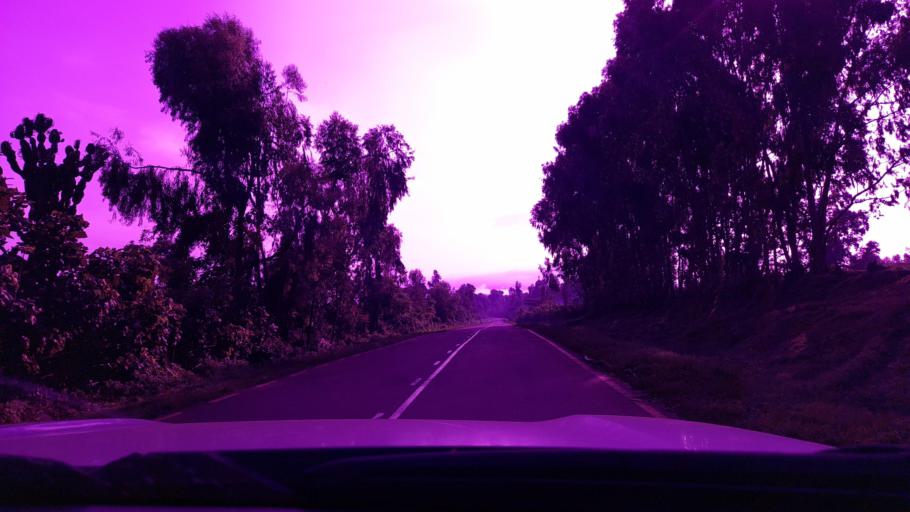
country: ET
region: Oromiya
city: Bedele
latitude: 8.1534
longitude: 36.4698
